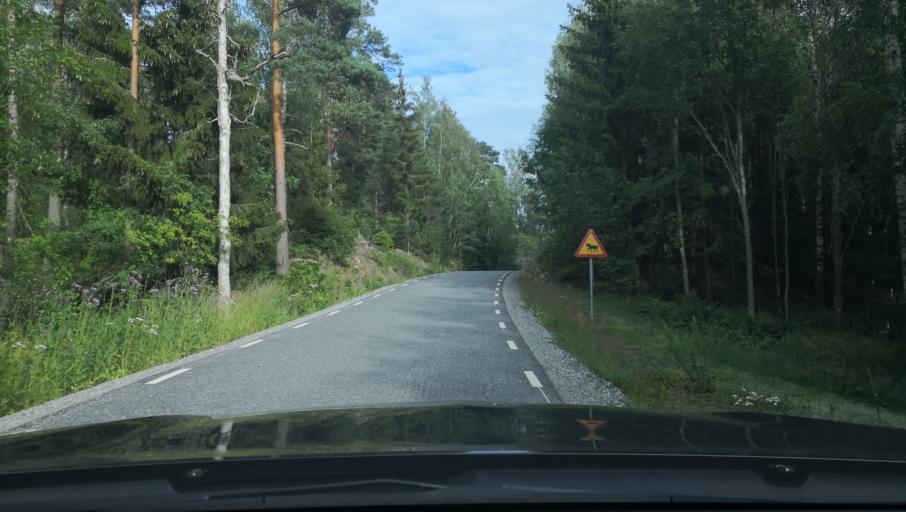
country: SE
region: Vaestmanland
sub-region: Surahammars Kommun
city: Surahammar
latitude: 59.6628
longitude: 16.1720
